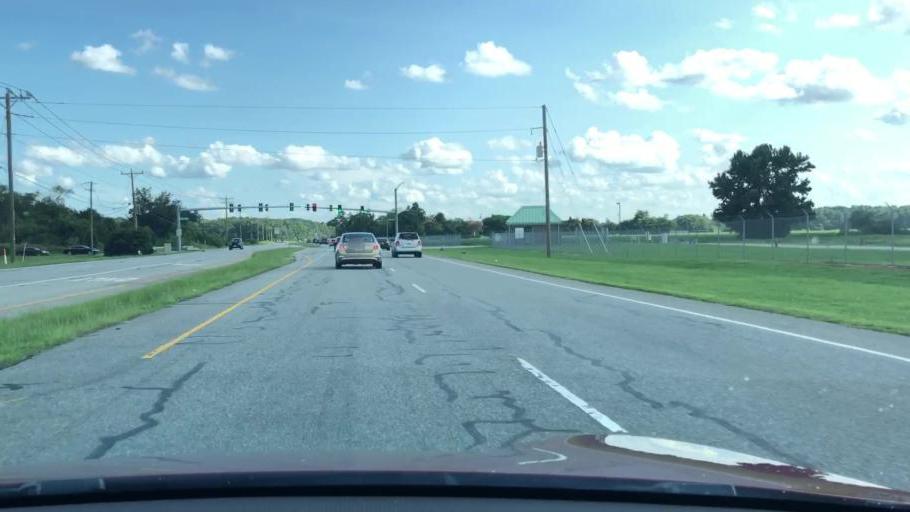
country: US
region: Virginia
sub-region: City of Virginia Beach
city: Virginia Beach
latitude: 36.8202
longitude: -76.0081
